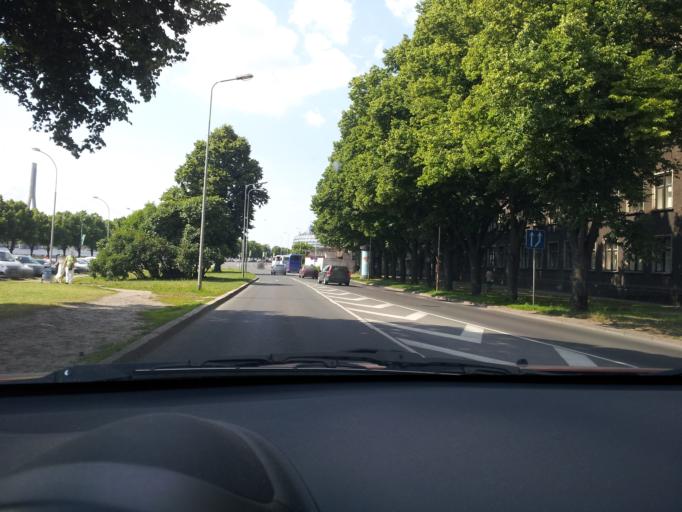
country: LV
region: Riga
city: Riga
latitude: 56.9468
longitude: 24.1046
